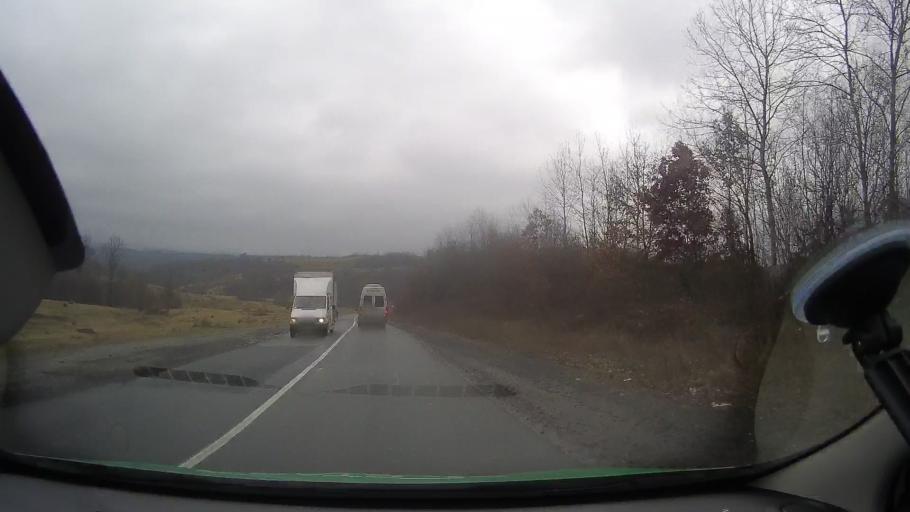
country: RO
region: Arad
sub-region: Comuna Varfurile
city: Varfurile
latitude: 46.2910
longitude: 22.5433
